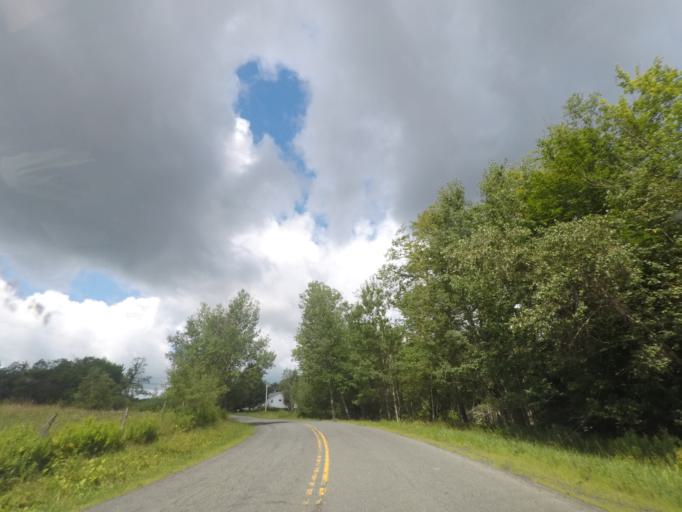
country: US
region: New York
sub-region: Rensselaer County
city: Averill Park
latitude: 42.6380
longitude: -73.4556
